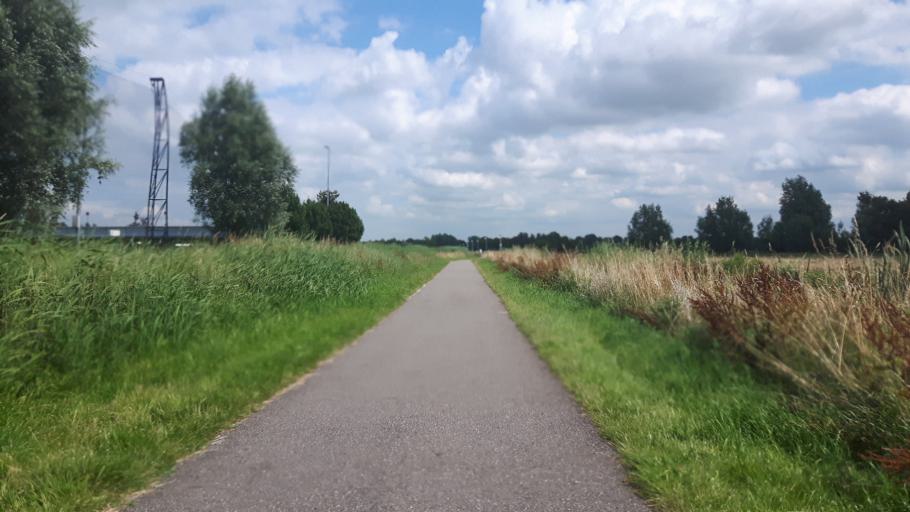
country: NL
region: South Holland
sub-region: Gemeente Krimpen aan den IJssel
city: Krimpen aan den IJssel
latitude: 51.9050
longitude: 4.6190
